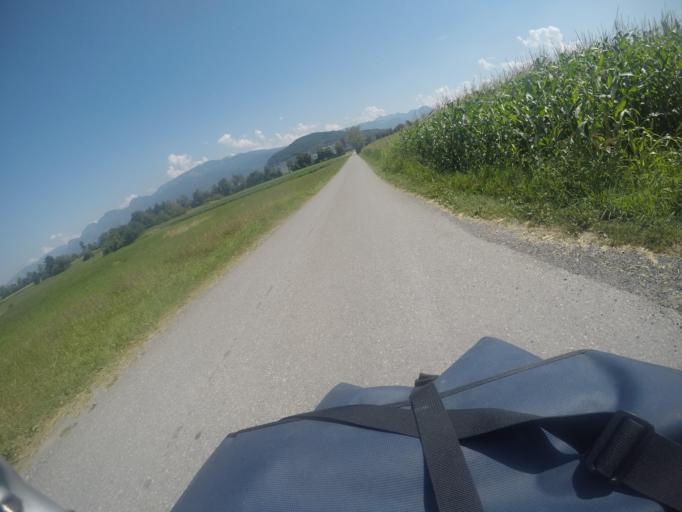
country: AT
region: Vorarlberg
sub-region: Politischer Bezirk Feldkirch
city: Koblach
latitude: 47.3498
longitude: 9.5832
